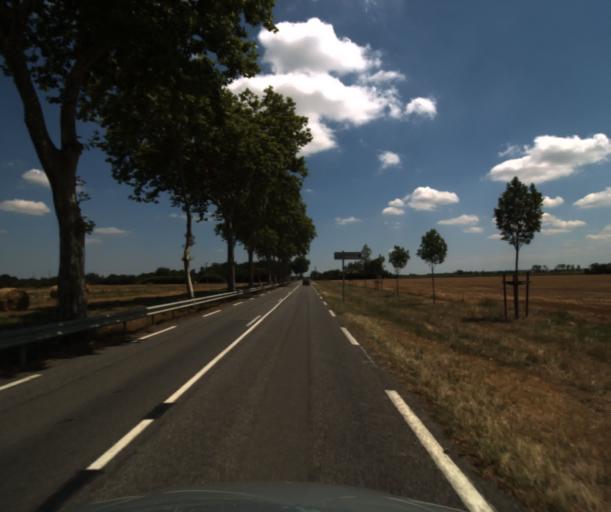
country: FR
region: Midi-Pyrenees
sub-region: Departement de la Haute-Garonne
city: Labastidette
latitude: 43.4682
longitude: 1.2324
